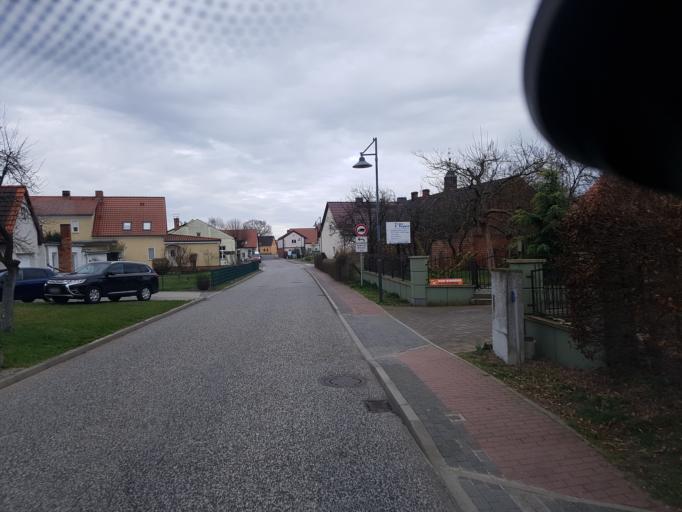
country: DE
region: Brandenburg
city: Mixdorf
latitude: 52.1963
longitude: 14.4066
